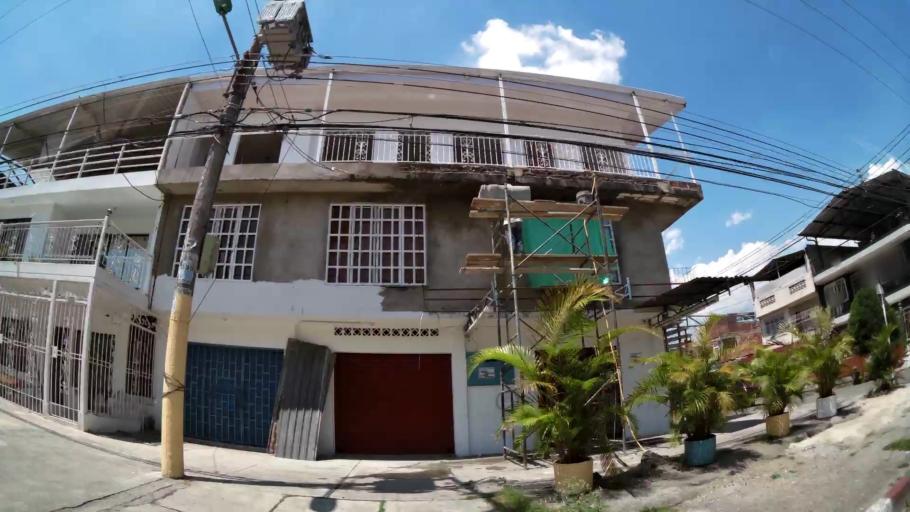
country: CO
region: Valle del Cauca
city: Cali
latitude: 3.4387
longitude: -76.4948
